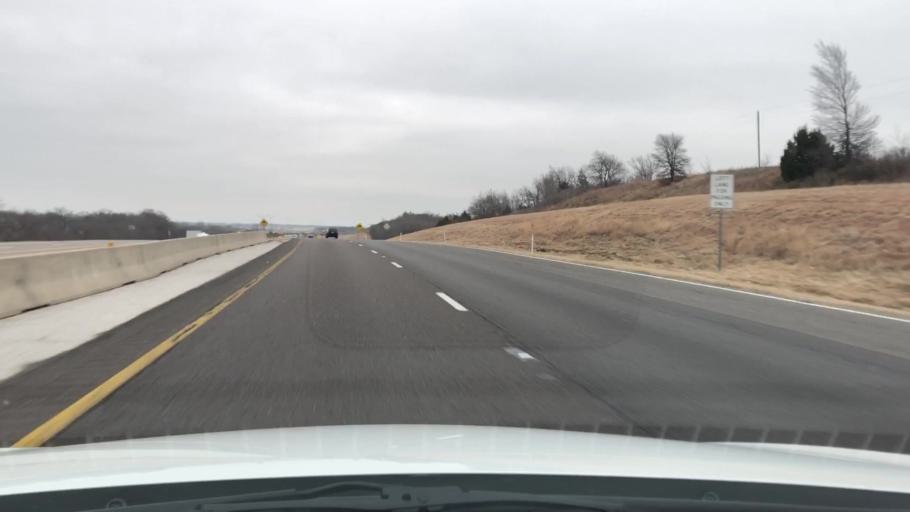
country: US
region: Texas
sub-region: Cooke County
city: Gainesville
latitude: 33.7187
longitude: -97.1609
